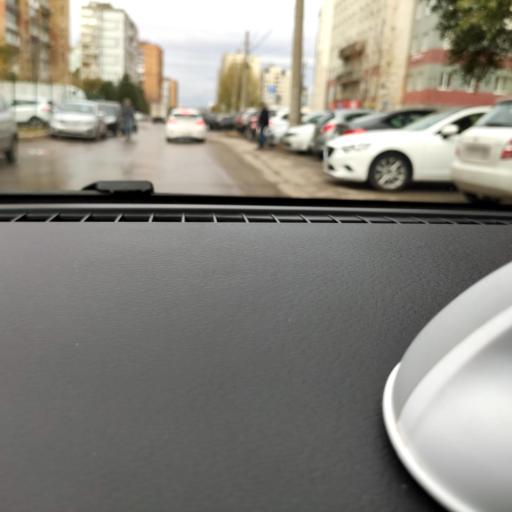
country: RU
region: Samara
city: Samara
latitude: 53.1977
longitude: 50.1456
